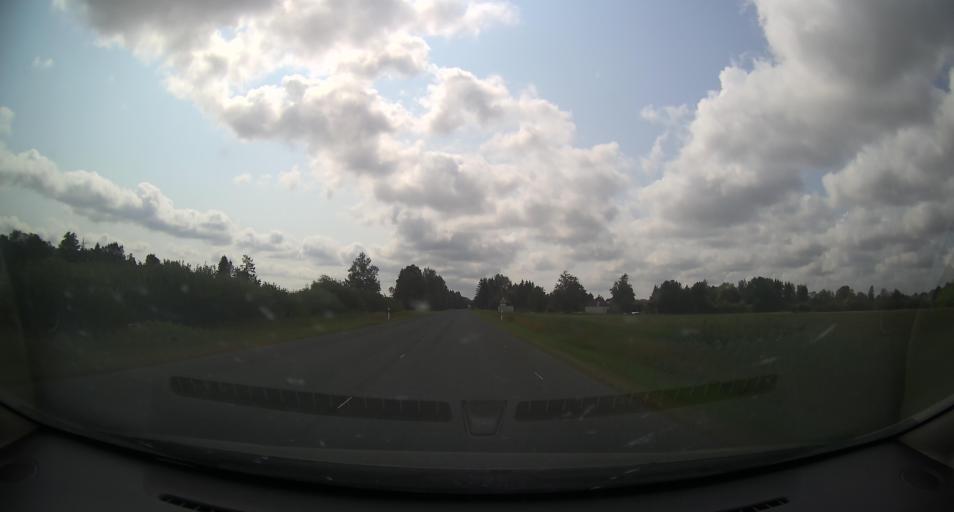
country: EE
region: Paernumaa
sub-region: Audru vald
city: Audru
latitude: 58.4776
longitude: 24.3296
